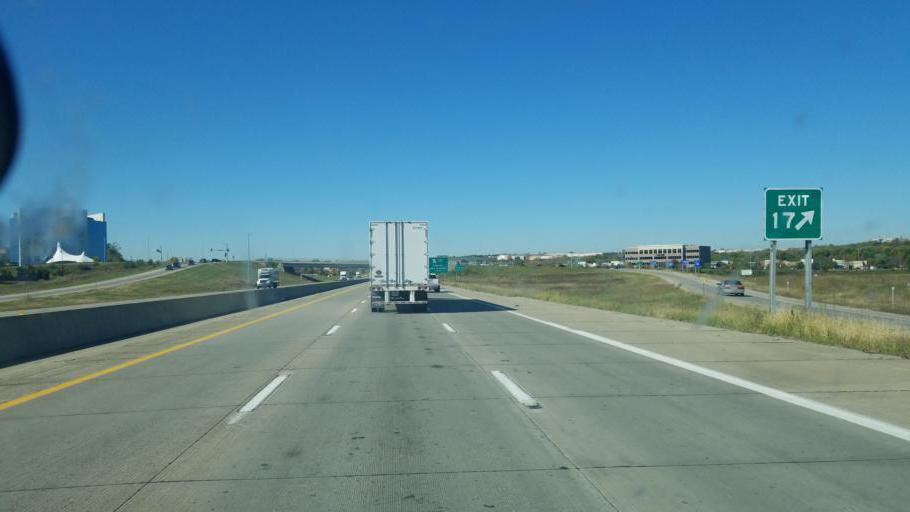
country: US
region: Missouri
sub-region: Jackson County
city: Blue Springs
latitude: 39.0384
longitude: -94.3367
